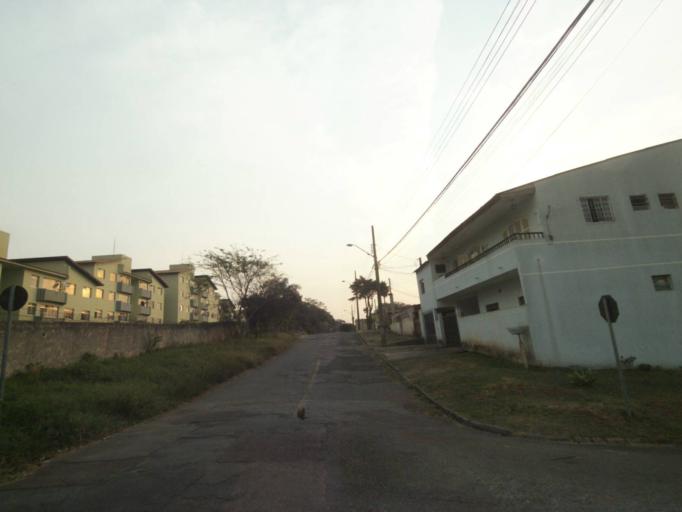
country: BR
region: Parana
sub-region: Curitiba
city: Curitiba
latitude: -25.4744
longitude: -49.2788
